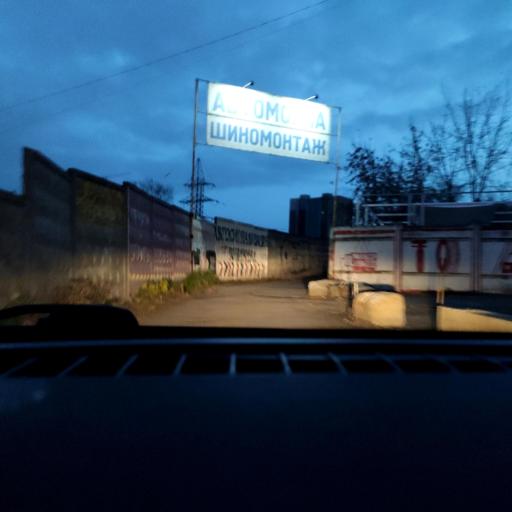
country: RU
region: Perm
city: Perm
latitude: 57.9936
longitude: 56.2118
